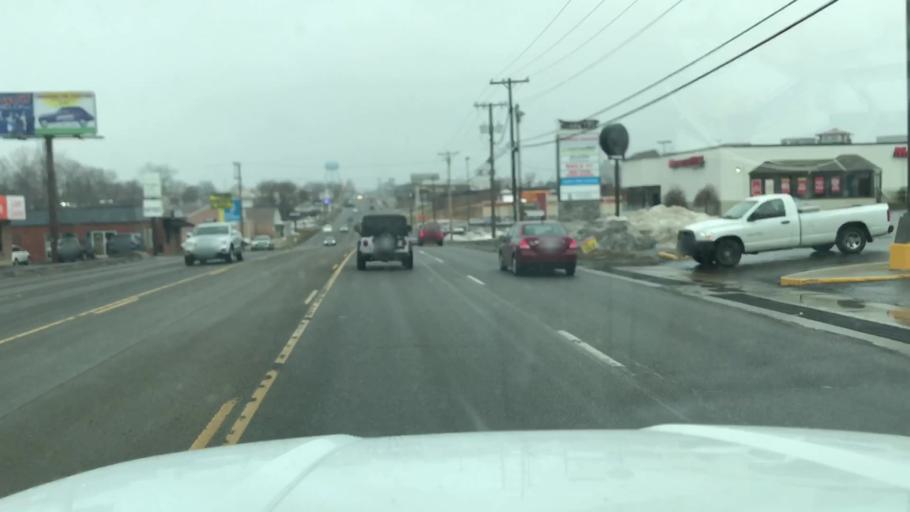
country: US
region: Missouri
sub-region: Buchanan County
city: Saint Joseph
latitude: 39.7717
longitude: -94.8034
